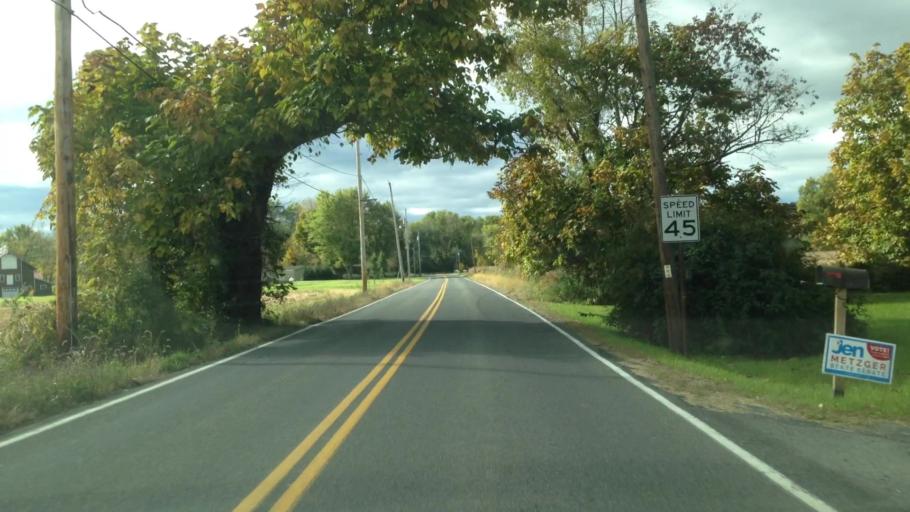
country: US
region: New York
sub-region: Ulster County
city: Tillson
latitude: 41.8101
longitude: -74.0801
